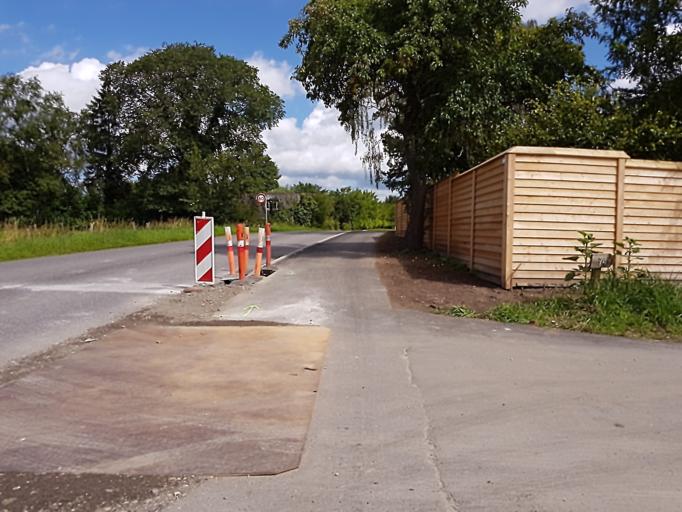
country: DK
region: Capital Region
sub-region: Egedal Kommune
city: Ganlose
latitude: 55.8050
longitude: 12.2833
